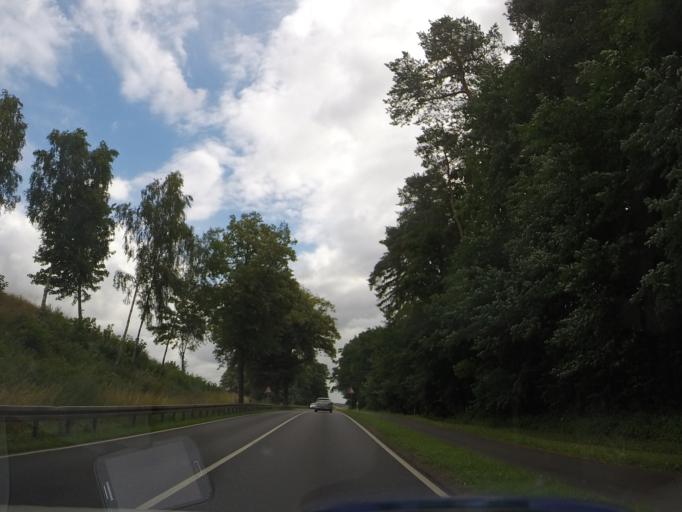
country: DE
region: Mecklenburg-Vorpommern
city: Lalendorf
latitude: 53.7703
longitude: 12.3352
